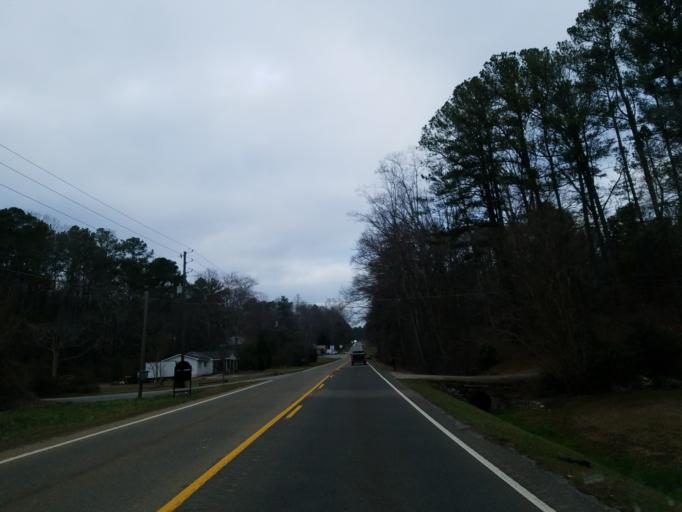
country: US
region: Georgia
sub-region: Cherokee County
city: Canton
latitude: 34.2754
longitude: -84.5068
